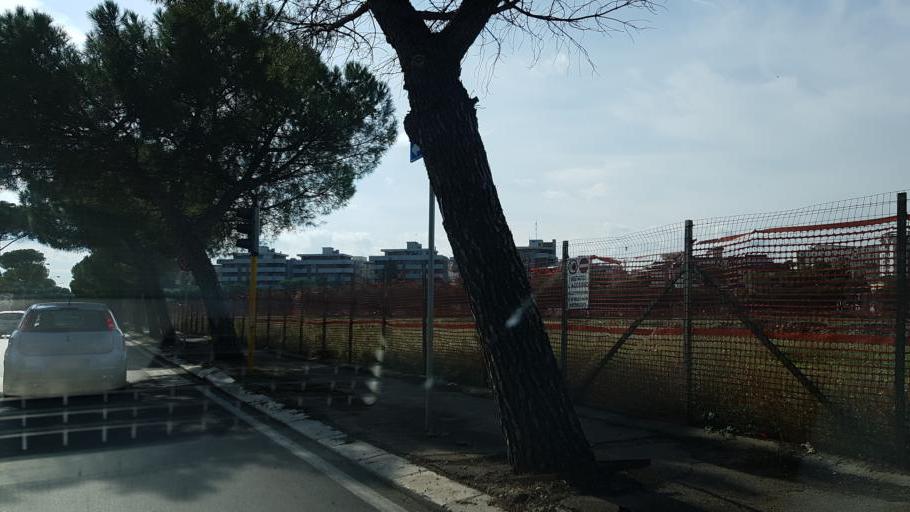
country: IT
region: Apulia
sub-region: Provincia di Foggia
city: Foggia
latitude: 41.4574
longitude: 15.5642
